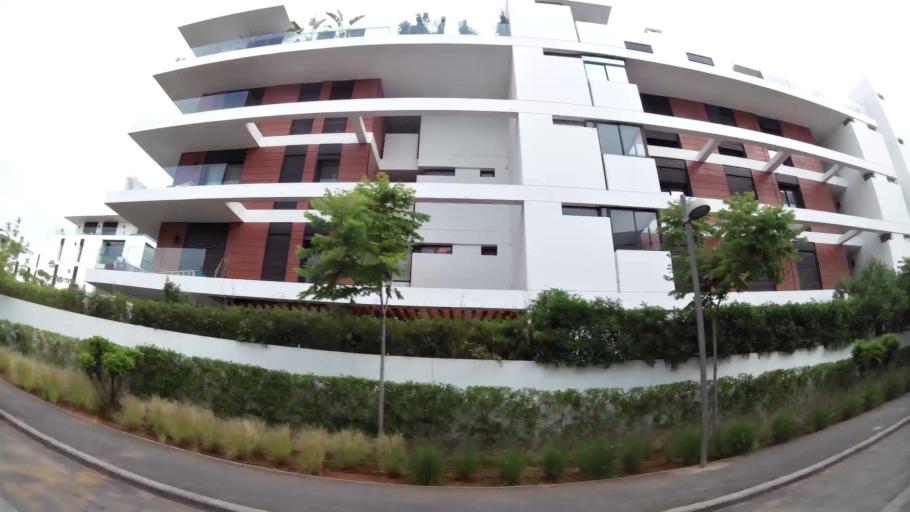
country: MA
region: Rabat-Sale-Zemmour-Zaer
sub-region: Rabat
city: Rabat
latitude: 33.9507
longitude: -6.8349
